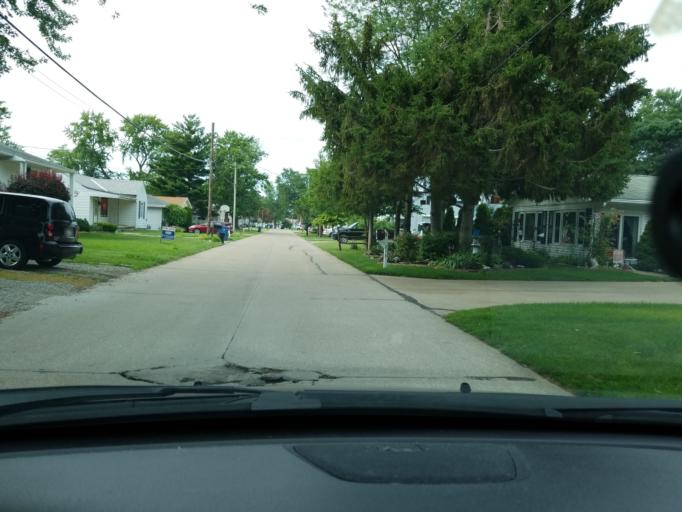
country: US
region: Ohio
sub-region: Erie County
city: Huron
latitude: 41.4091
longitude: -82.5906
